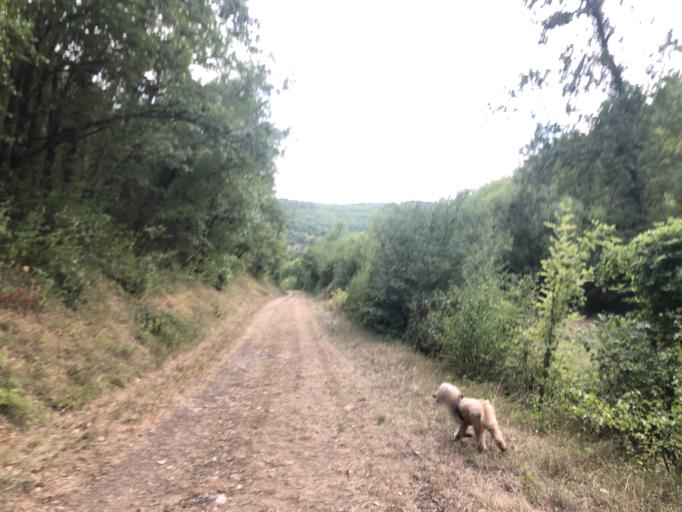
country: FR
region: Aquitaine
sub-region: Departement de la Dordogne
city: Cenac-et-Saint-Julien
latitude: 44.7575
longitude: 1.1992
